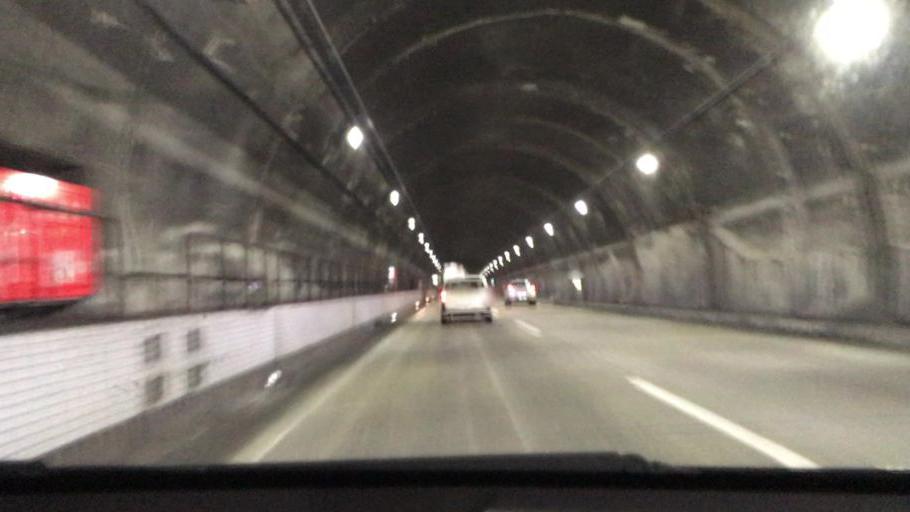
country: JP
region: Yamaguchi
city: Tokuyama
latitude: 34.0724
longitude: 131.7112
